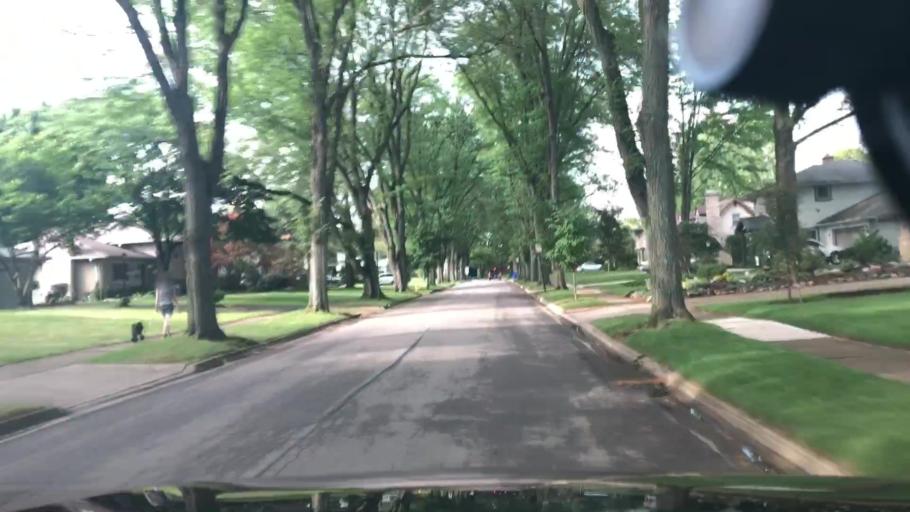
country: US
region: Ohio
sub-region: Franklin County
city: Upper Arlington
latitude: 40.0174
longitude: -83.0519
